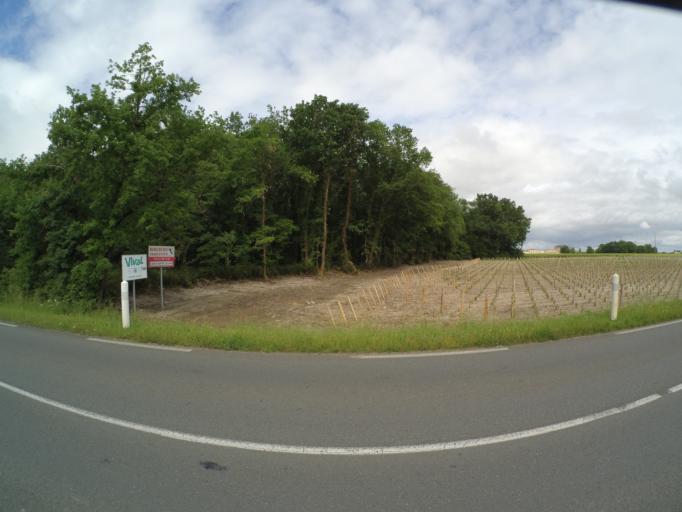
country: FR
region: Aquitaine
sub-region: Departement de la Gironde
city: Soussans
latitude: 45.0513
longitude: -0.6938
